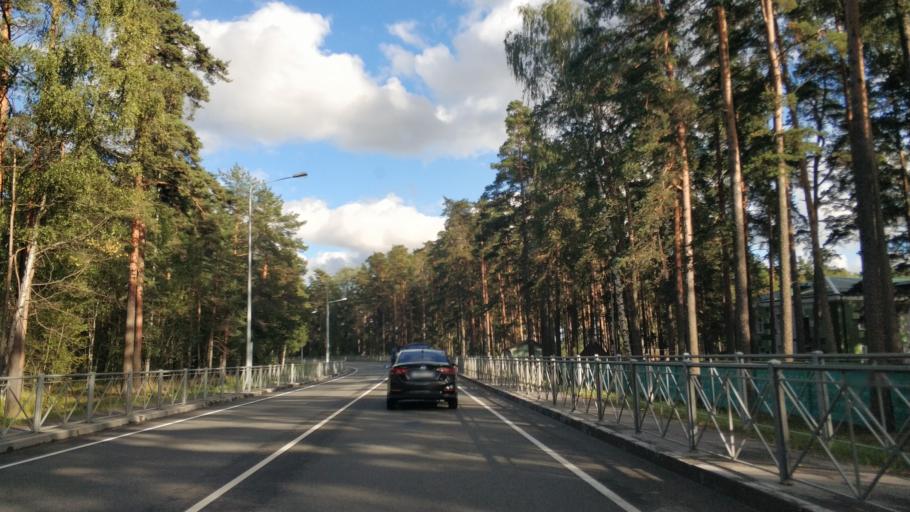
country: RU
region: Leningrad
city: Priozersk
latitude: 61.0101
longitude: 30.1627
